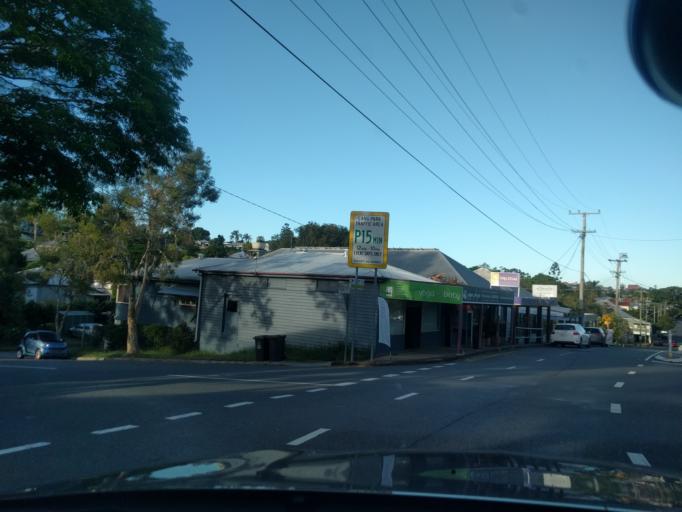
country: AU
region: Queensland
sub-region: Brisbane
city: Milton
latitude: -27.4708
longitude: 152.9957
